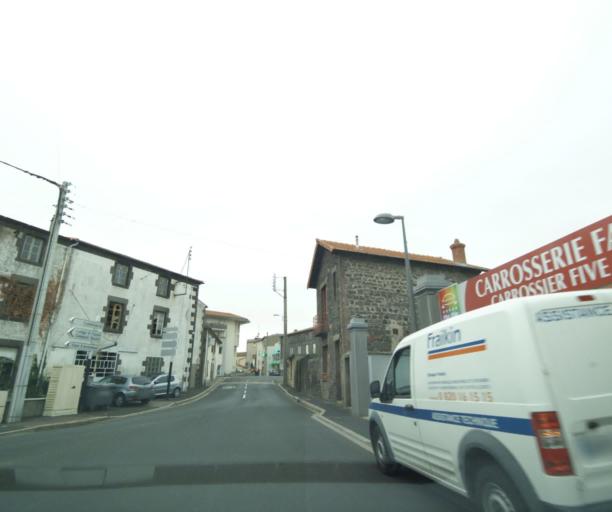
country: FR
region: Auvergne
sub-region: Departement du Puy-de-Dome
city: Gerzat
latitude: 45.8260
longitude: 3.1456
